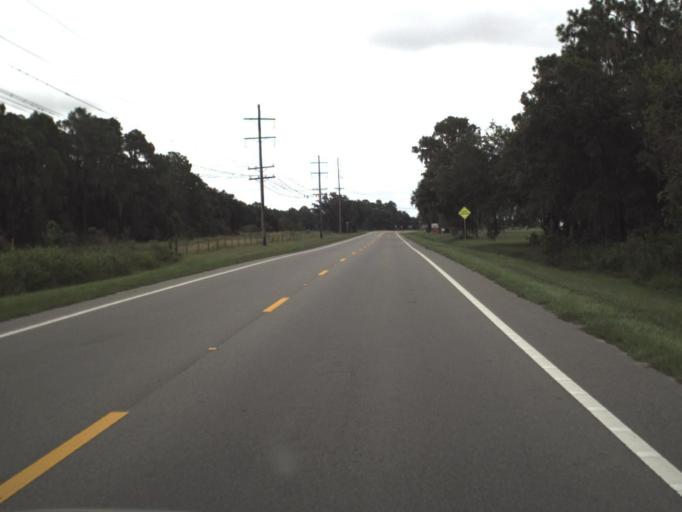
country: US
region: Florida
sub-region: Hillsborough County
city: Wimauma
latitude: 27.5901
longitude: -82.1262
